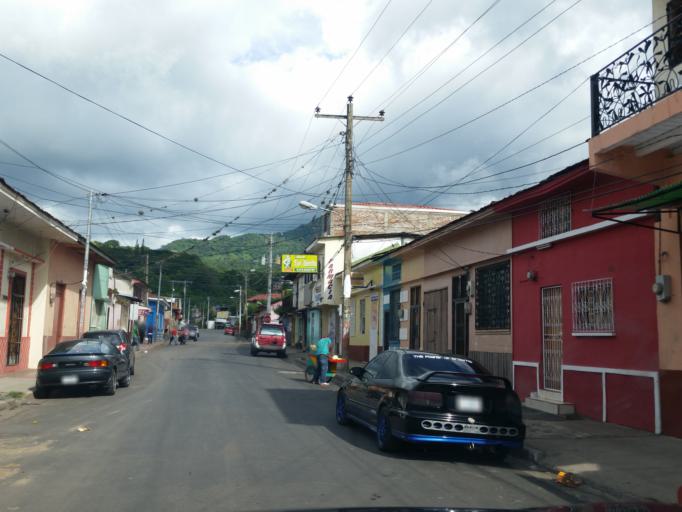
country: NI
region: Matagalpa
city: Matagalpa
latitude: 12.9296
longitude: -85.9153
